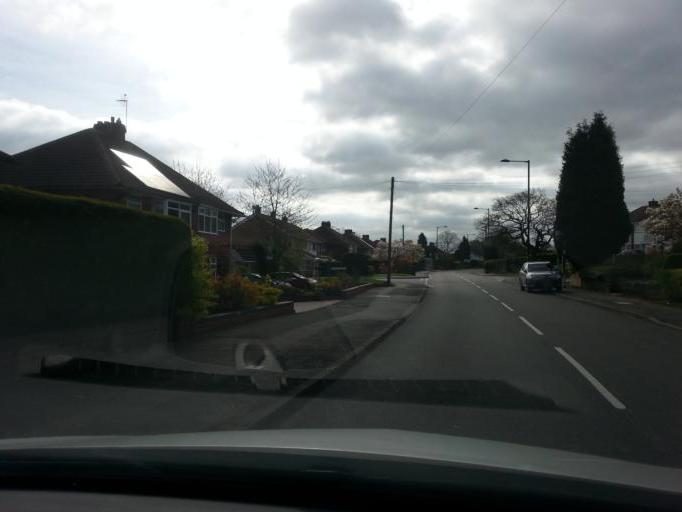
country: GB
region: England
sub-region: Staffordshire
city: Shenstone
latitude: 52.5971
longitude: -1.8457
